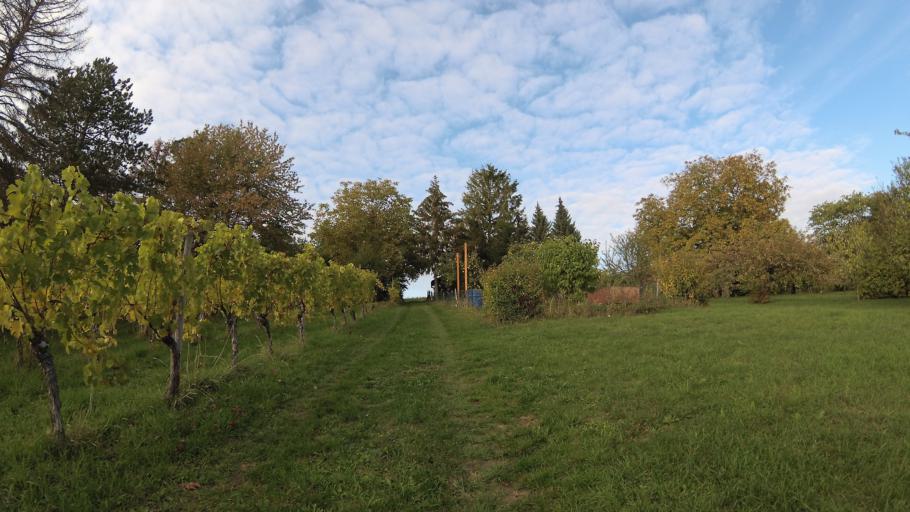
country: DE
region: Baden-Wuerttemberg
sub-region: Regierungsbezirk Stuttgart
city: Neckarsulm
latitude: 49.1931
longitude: 9.2415
